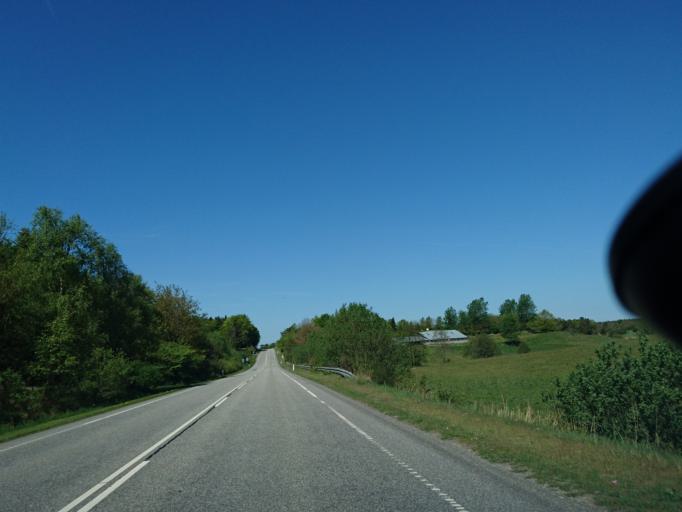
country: DK
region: North Denmark
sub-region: Hjorring Kommune
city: Sindal
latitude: 57.4640
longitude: 10.2821
